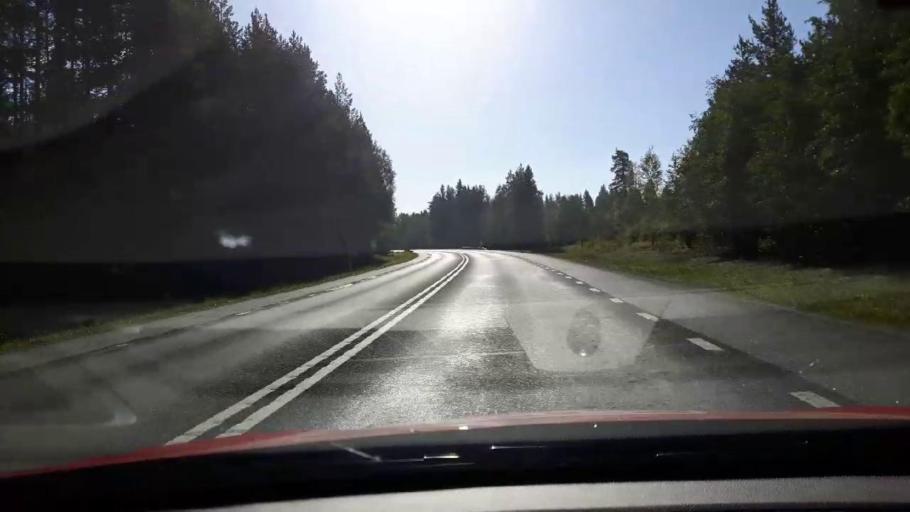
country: SE
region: Jaemtland
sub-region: Braecke Kommun
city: Braecke
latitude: 62.7164
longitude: 15.4579
